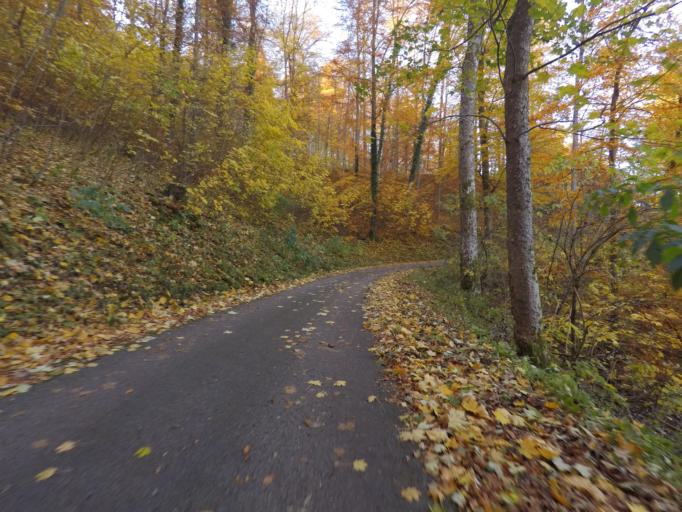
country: DE
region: Baden-Wuerttemberg
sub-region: Tuebingen Region
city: Pfullingen
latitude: 48.4431
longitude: 9.2282
